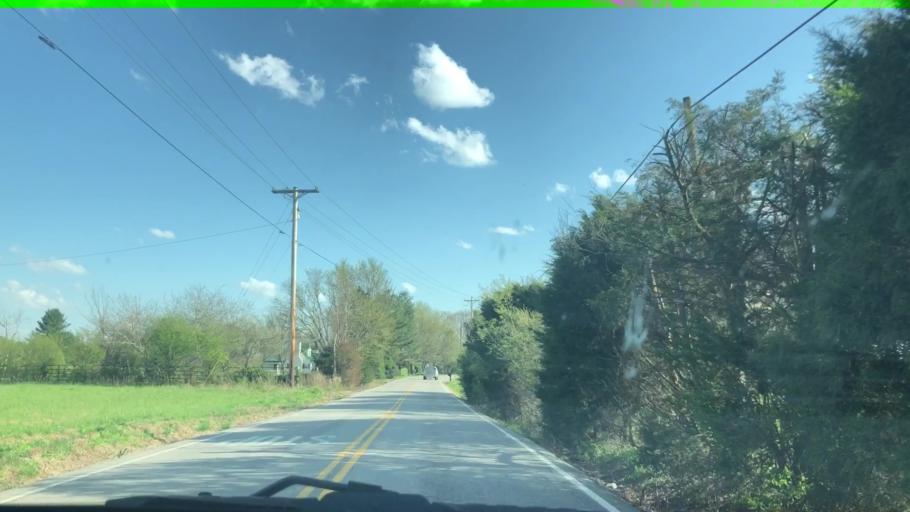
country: US
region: Tennessee
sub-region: Putnam County
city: Baxter
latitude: 36.0871
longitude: -85.5849
